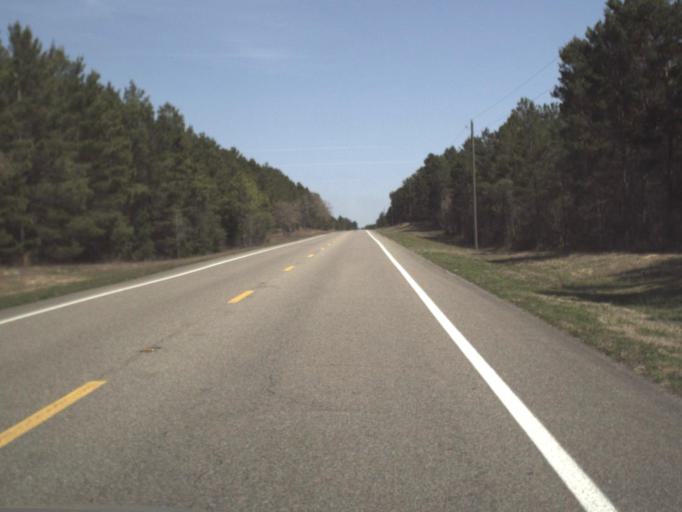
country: US
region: Florida
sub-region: Liberty County
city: Bristol
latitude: 30.4946
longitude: -84.8953
